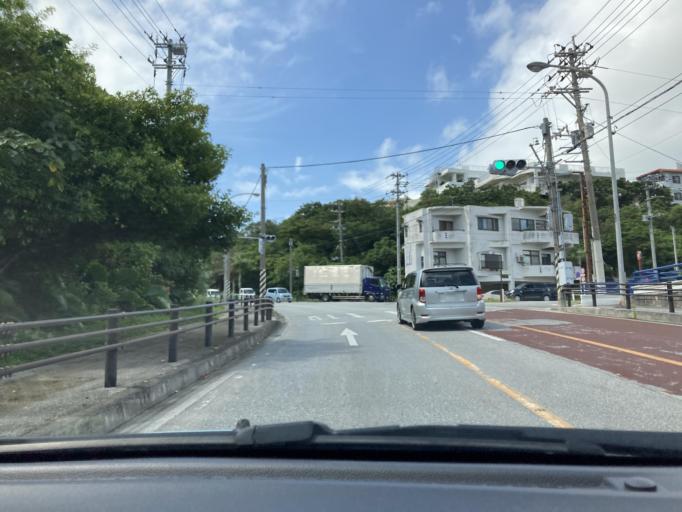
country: JP
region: Okinawa
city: Chatan
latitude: 26.3014
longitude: 127.8020
